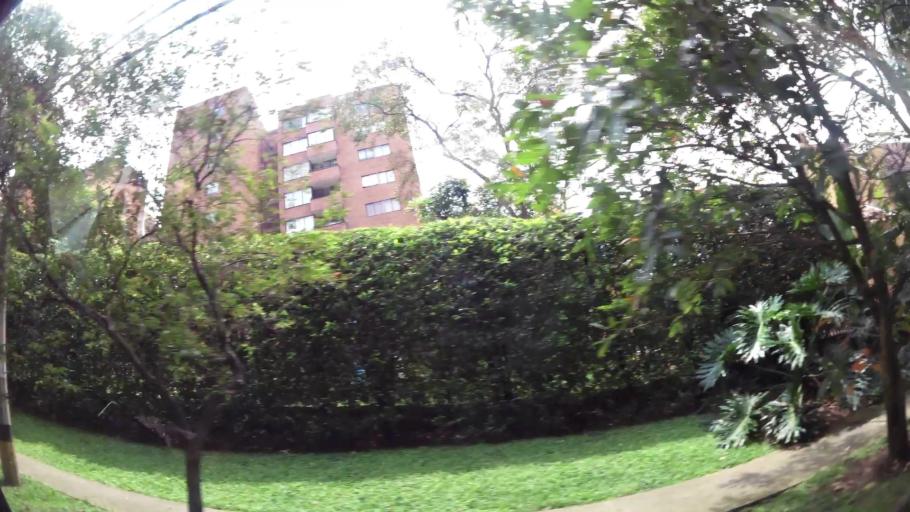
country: CO
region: Antioquia
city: Envigado
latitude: 6.1809
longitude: -75.5731
